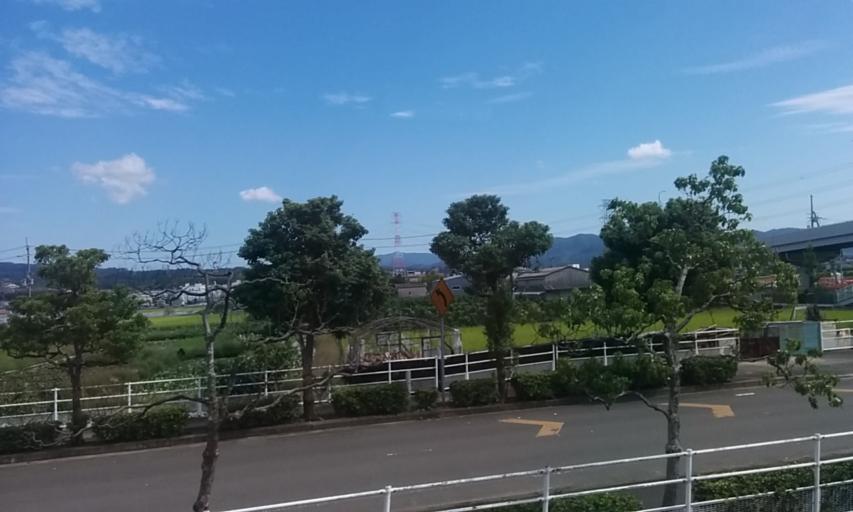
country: JP
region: Kyoto
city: Tanabe
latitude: 34.8473
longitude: 135.7722
